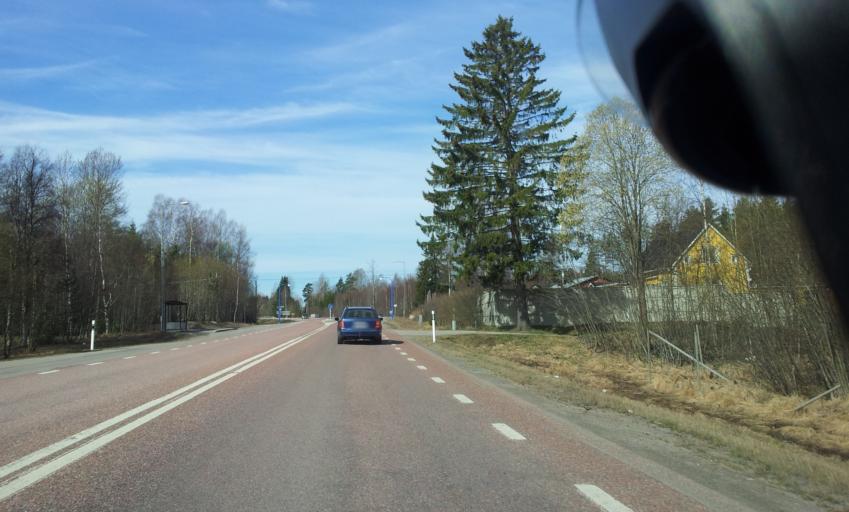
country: SE
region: Gaevleborg
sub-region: Hudiksvalls Kommun
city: Hudiksvall
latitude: 61.7143
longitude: 17.0664
